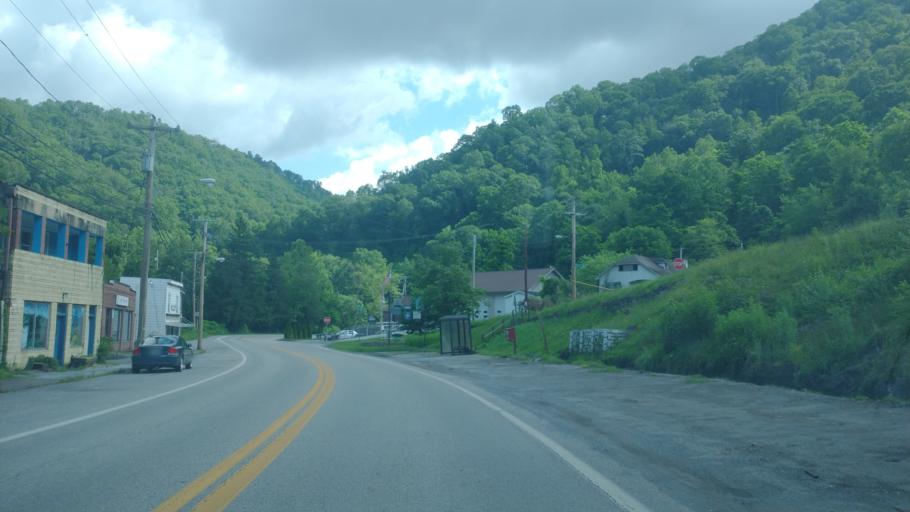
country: US
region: West Virginia
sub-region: McDowell County
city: Welch
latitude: 37.4273
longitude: -81.5065
